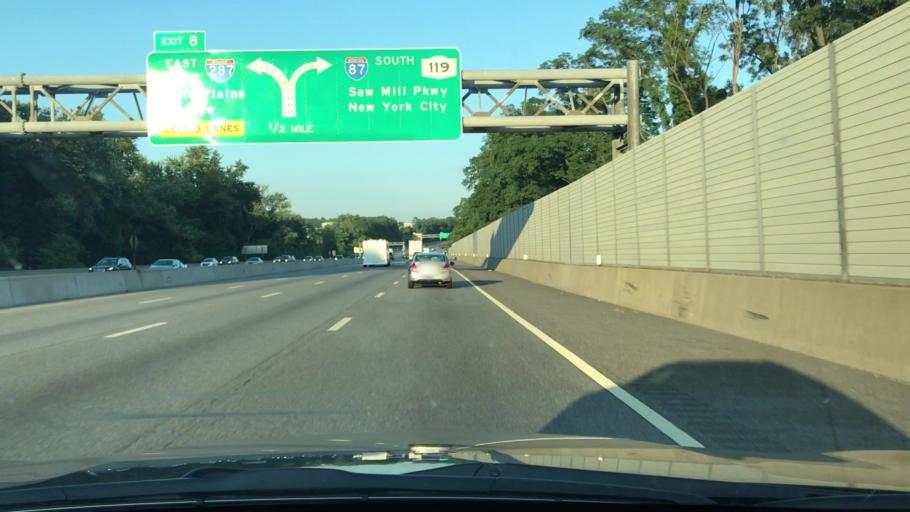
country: US
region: New York
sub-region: Westchester County
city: Tarrytown
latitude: 41.0607
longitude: -73.8512
